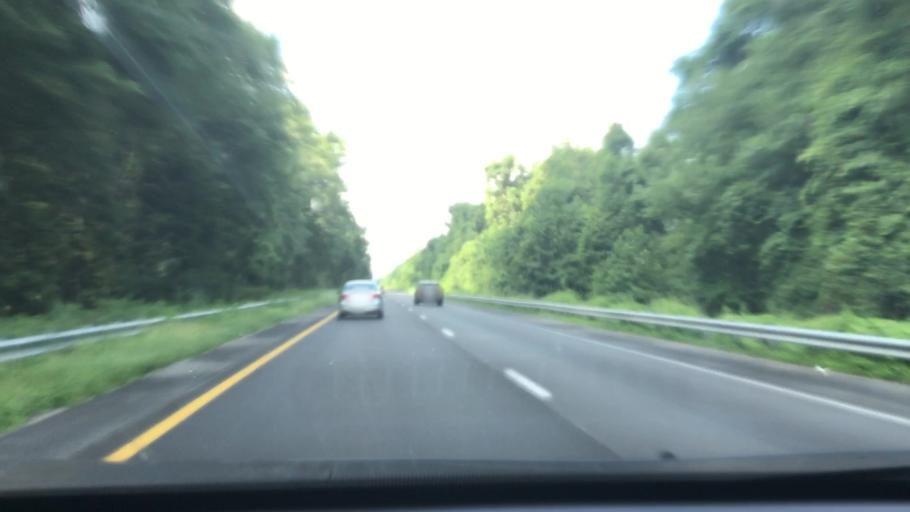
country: US
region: South Carolina
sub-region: Clarendon County
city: Manning
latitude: 33.8283
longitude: -80.1347
